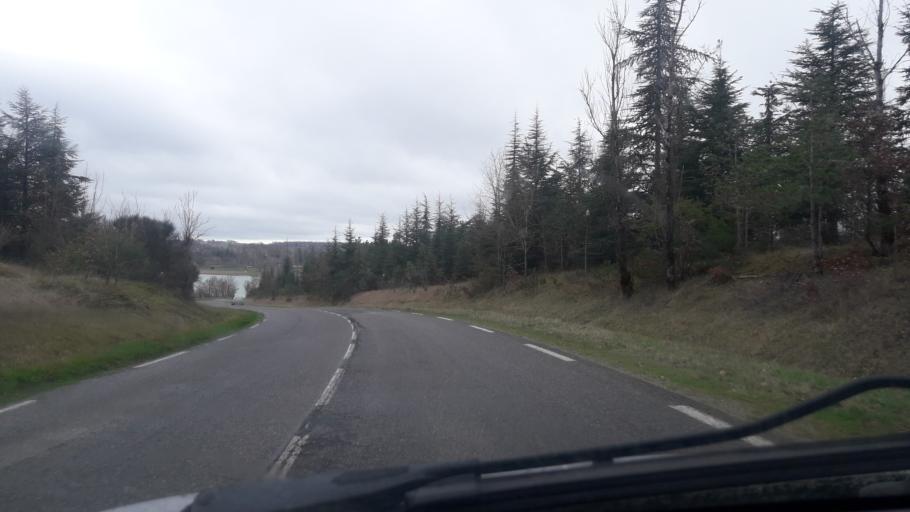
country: FR
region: Midi-Pyrenees
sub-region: Departement du Gers
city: Gimont
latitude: 43.6939
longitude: 0.9971
